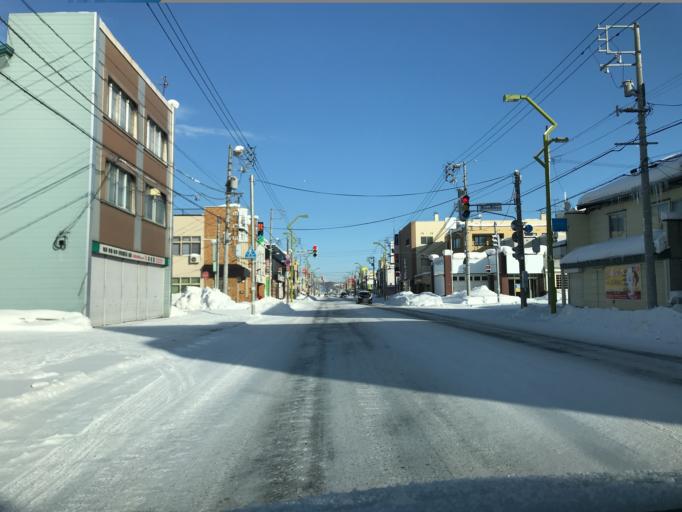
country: JP
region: Hokkaido
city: Nayoro
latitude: 44.3501
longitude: 142.4572
